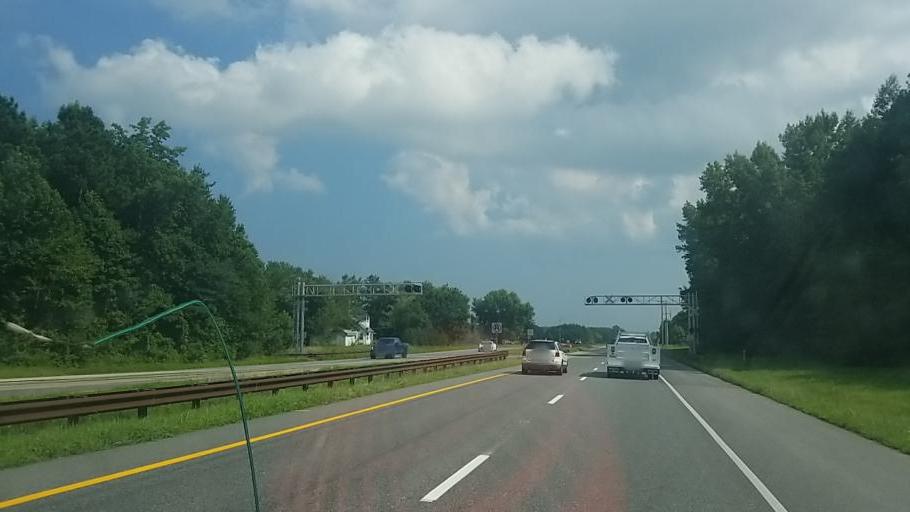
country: US
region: Delaware
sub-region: Sussex County
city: Selbyville
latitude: 38.4359
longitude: -75.2238
